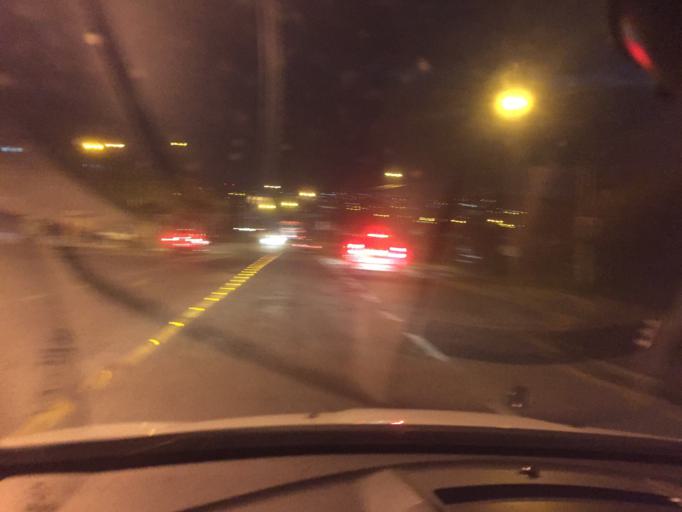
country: BR
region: Sao Paulo
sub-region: Campo Limpo Paulista
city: Campo Limpo Paulista
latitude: -23.2066
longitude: -46.8023
